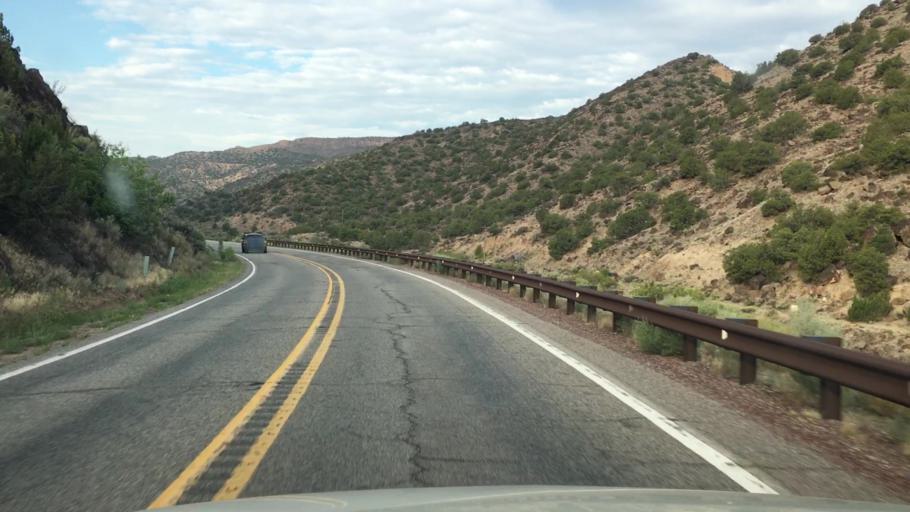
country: US
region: New Mexico
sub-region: Rio Arriba County
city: Ohkay Owingeh
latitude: 36.2027
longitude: -105.9678
